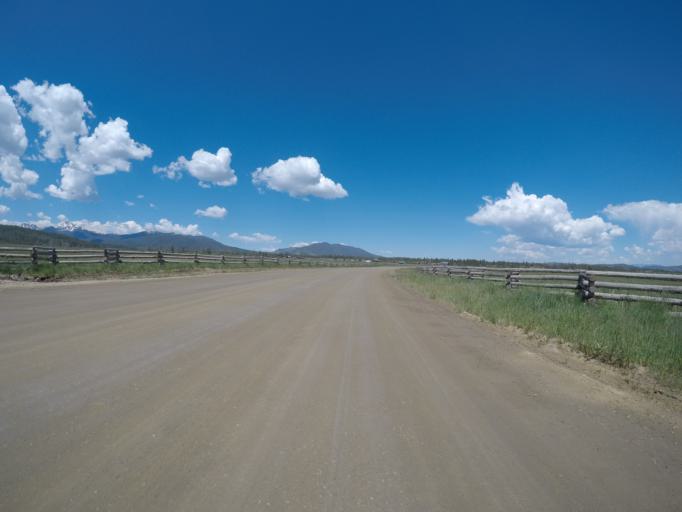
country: US
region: Colorado
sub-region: Grand County
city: Fraser
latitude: 39.9402
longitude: -105.8207
